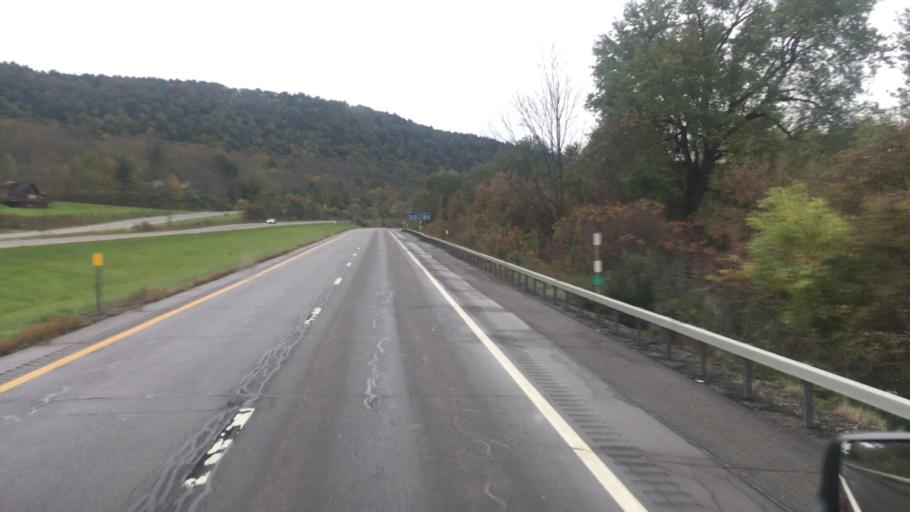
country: US
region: New York
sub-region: Tioga County
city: Owego
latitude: 42.0814
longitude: -76.2149
